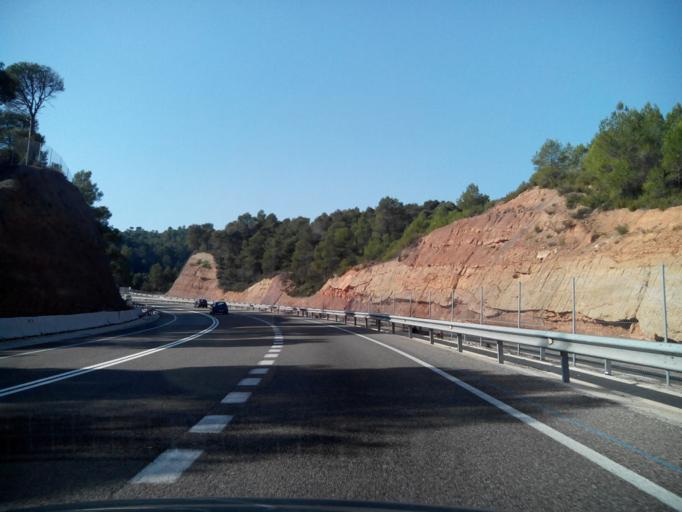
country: ES
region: Catalonia
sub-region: Provincia de Barcelona
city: Castellfollit del Boix
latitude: 41.6537
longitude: 1.7090
